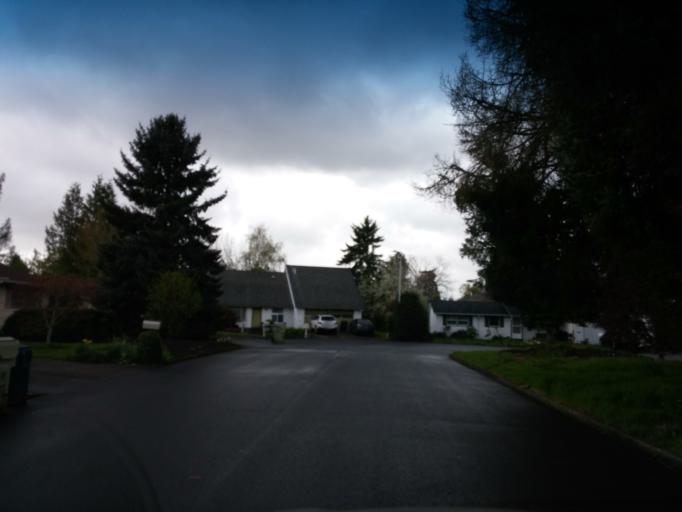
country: US
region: Oregon
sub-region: Washington County
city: Aloha
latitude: 45.5021
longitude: -122.8652
